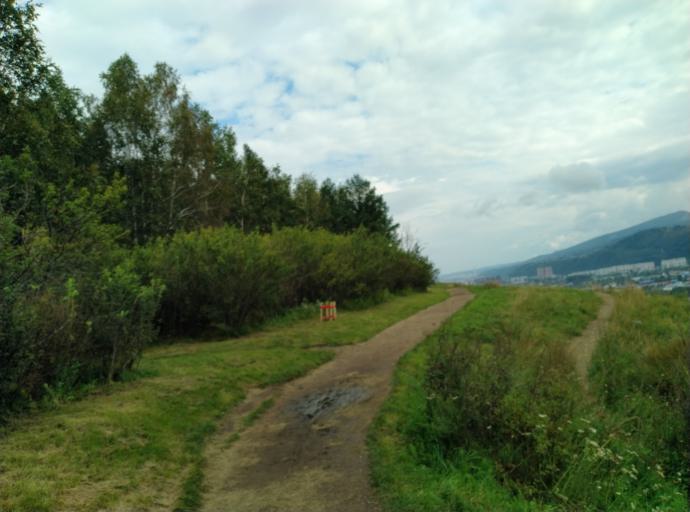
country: RU
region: Krasnoyarskiy
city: Krasnoyarsk
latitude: 55.9830
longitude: 92.7525
